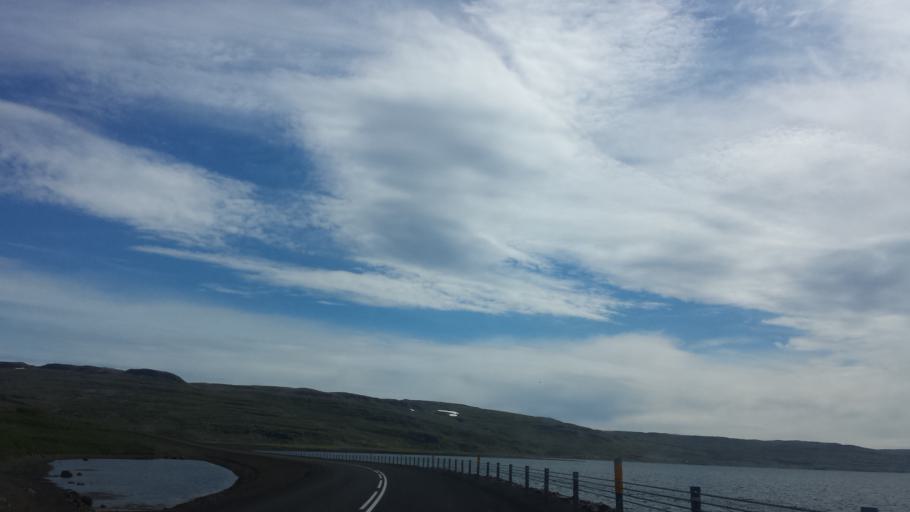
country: IS
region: West
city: Stykkisholmur
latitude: 65.7712
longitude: -21.7559
